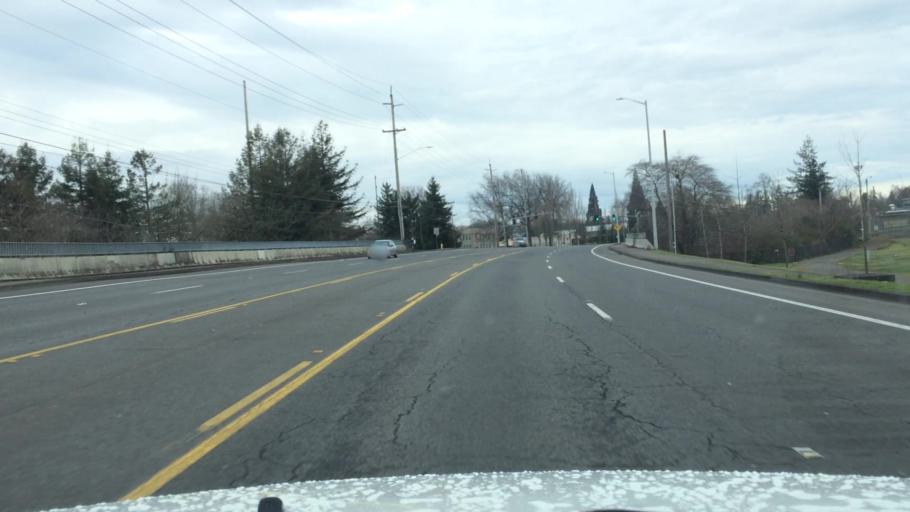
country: US
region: Oregon
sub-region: Marion County
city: Four Corners
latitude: 44.9284
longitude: -123.0014
